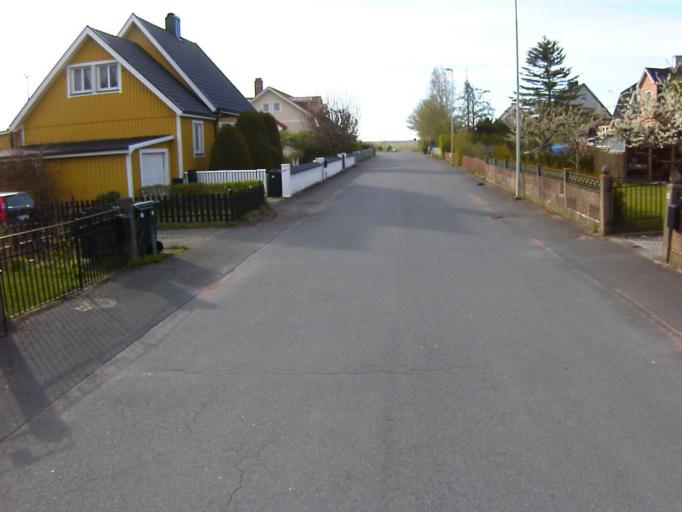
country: SE
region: Skane
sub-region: Kristianstads Kommun
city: Kristianstad
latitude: 56.0611
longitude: 14.1671
